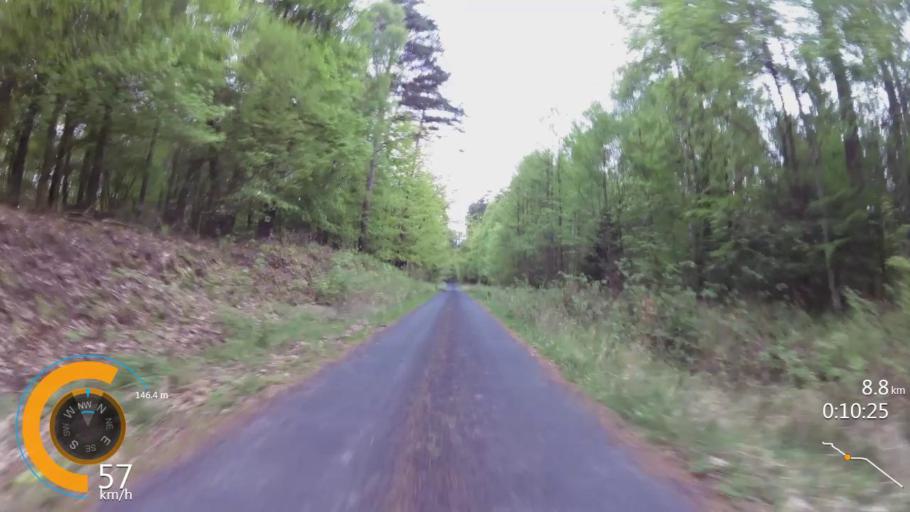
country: PL
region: West Pomeranian Voivodeship
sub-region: Powiat drawski
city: Wierzchowo
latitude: 53.5055
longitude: 16.1236
